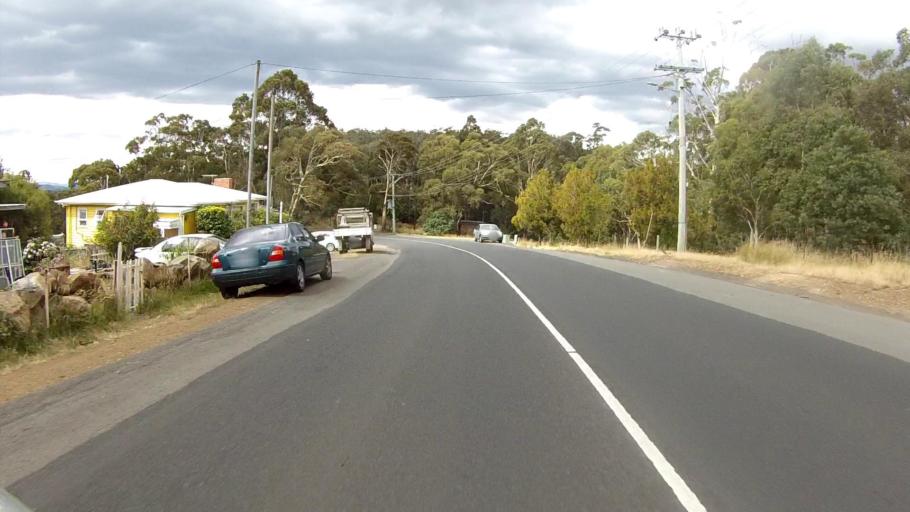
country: AU
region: Tasmania
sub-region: Hobart
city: Dynnyrne
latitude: -42.9040
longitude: 147.2882
